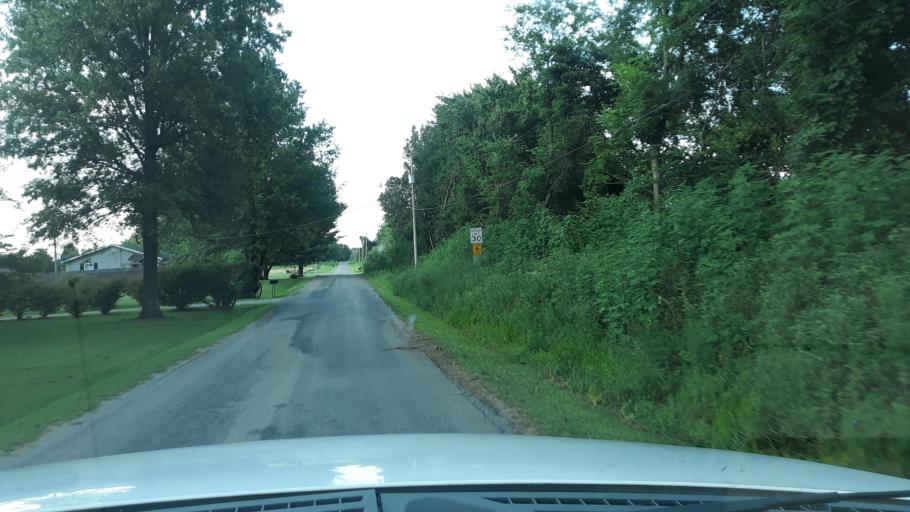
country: US
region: Illinois
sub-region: Saline County
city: Eldorado
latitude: 37.8253
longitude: -88.5166
